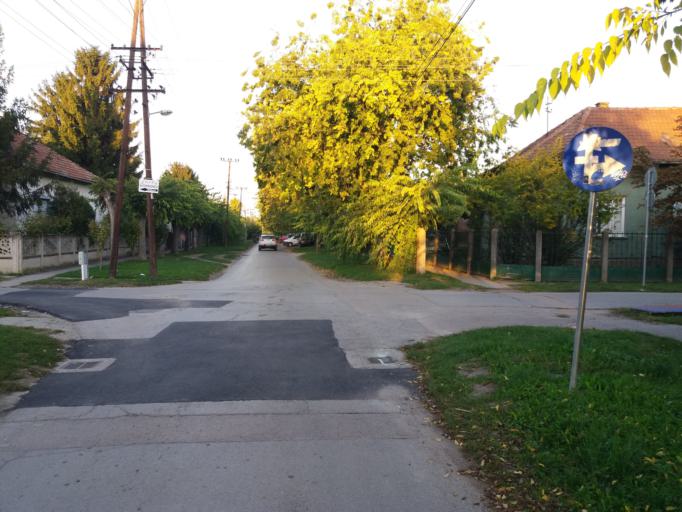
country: RS
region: Autonomna Pokrajina Vojvodina
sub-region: Severnobacki Okrug
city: Subotica
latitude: 46.1022
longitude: 19.6821
